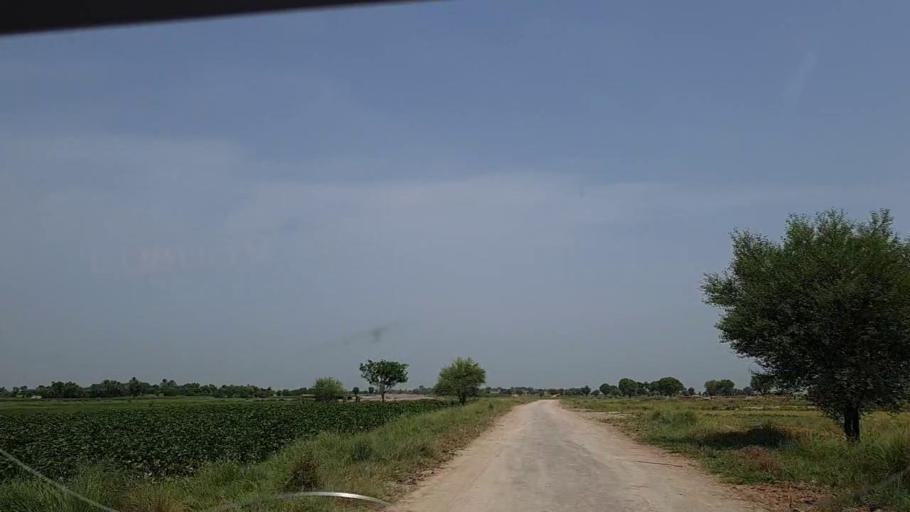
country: PK
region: Sindh
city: Tharu Shah
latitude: 26.9153
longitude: 68.0564
